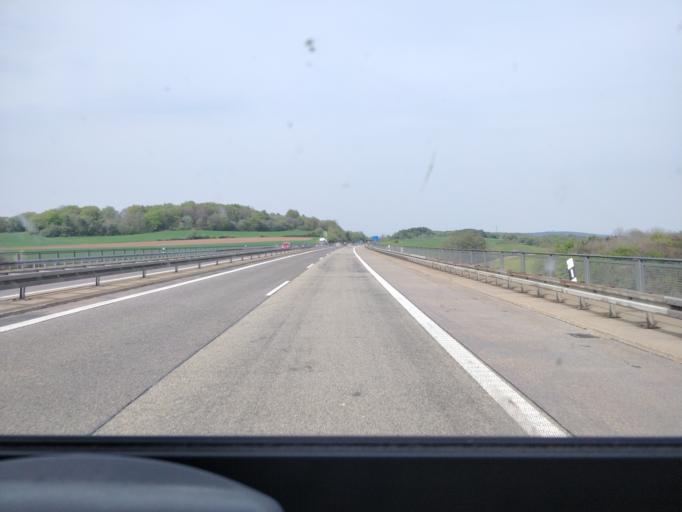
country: DE
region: North Rhine-Westphalia
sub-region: Regierungsbezirk Koln
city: Nettersheim
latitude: 50.5186
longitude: 6.6653
